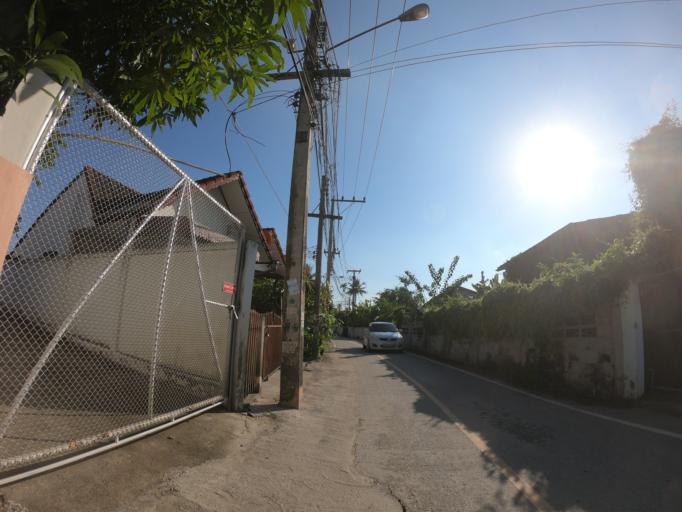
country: TH
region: Chiang Mai
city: San Sai
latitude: 18.8324
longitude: 99.0339
